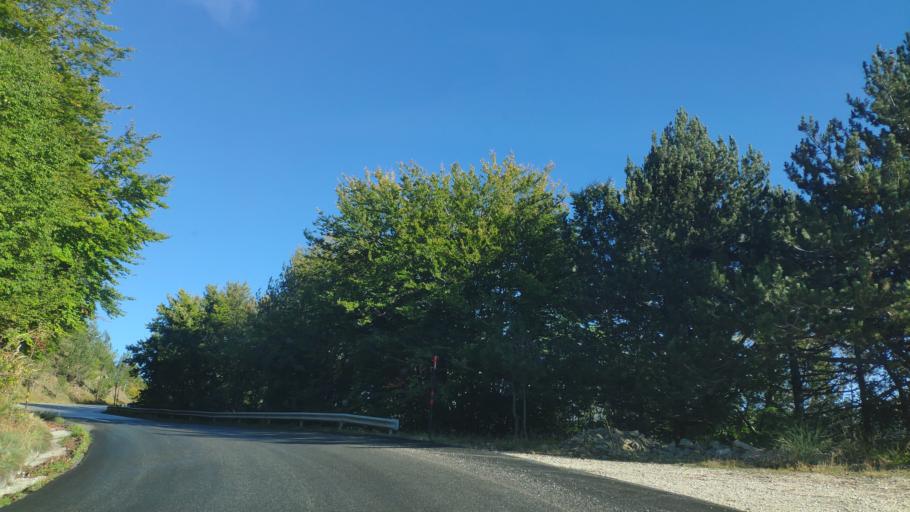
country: GR
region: Epirus
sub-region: Nomos Ioanninon
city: Metsovo
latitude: 39.7749
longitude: 21.1768
